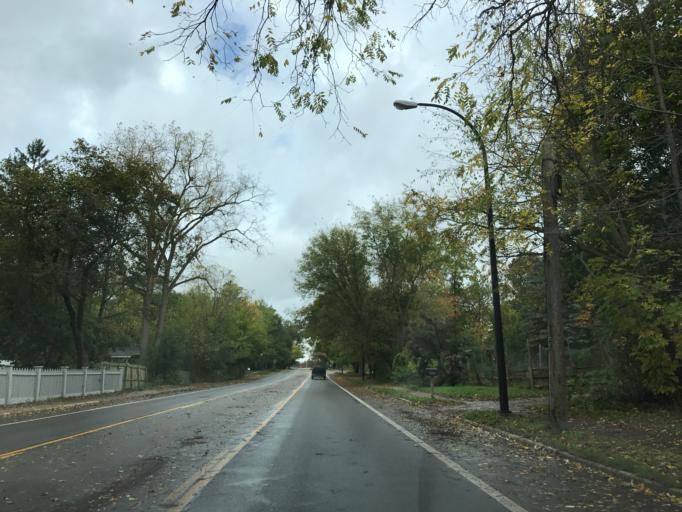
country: US
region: Michigan
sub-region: Washtenaw County
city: Ann Arbor
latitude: 42.2456
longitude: -83.7166
